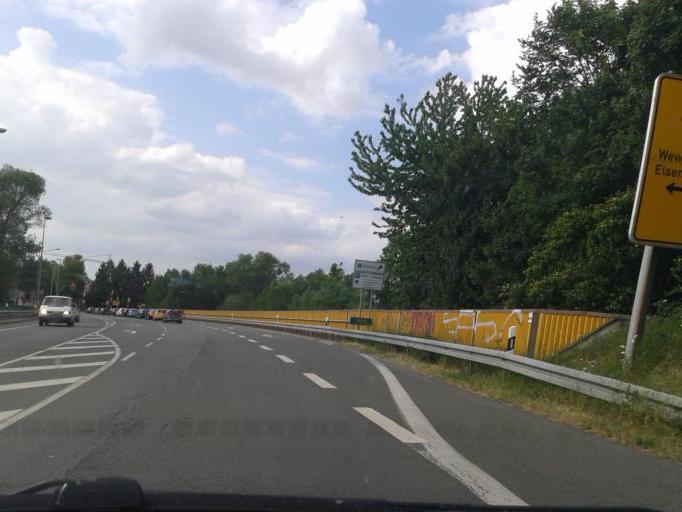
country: DE
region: North Rhine-Westphalia
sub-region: Regierungsbezirk Detmold
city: Paderborn
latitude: 51.7408
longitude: 8.7108
